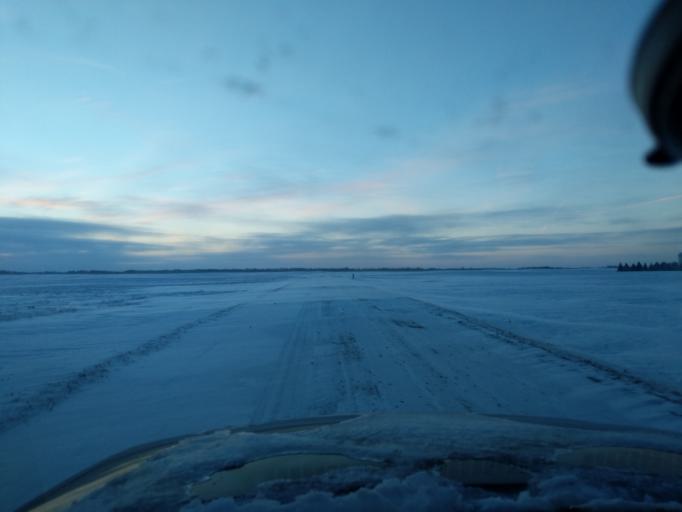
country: US
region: Minnesota
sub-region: Renville County
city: Renville
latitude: 44.7271
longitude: -95.3525
